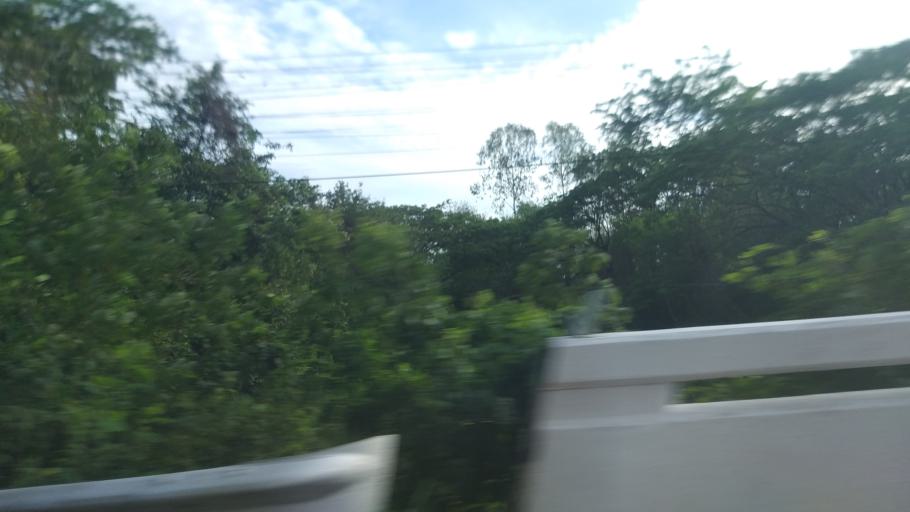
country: TH
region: Chaiyaphum
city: Ban Thaen
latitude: 16.3827
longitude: 102.3077
